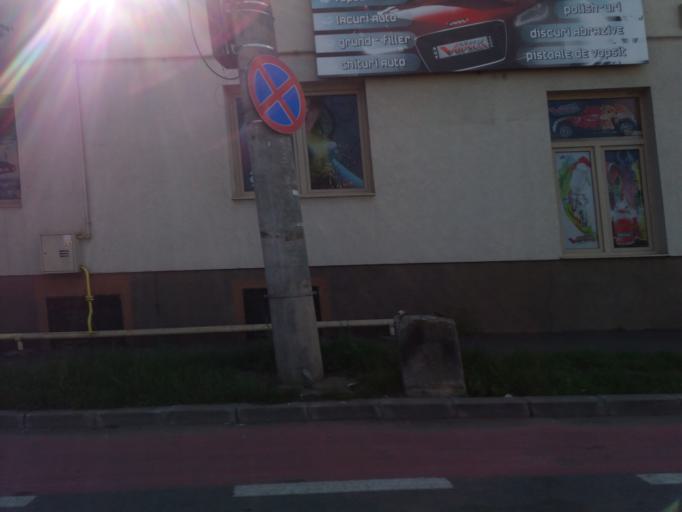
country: RO
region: Arad
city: Arad
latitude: 46.1750
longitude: 21.3062
